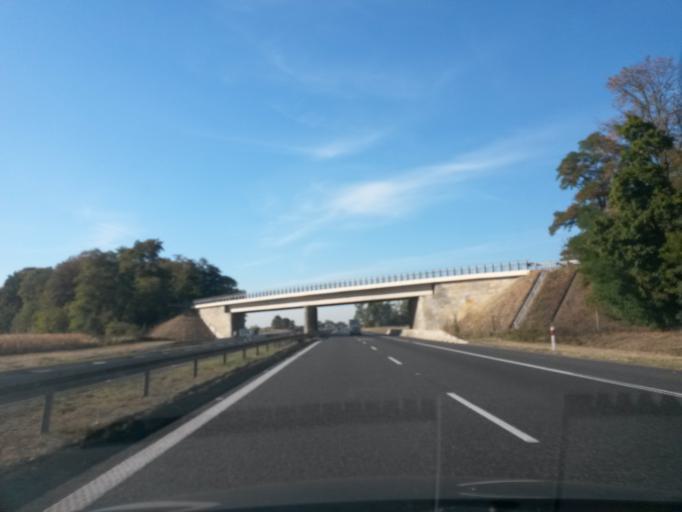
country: PL
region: Lower Silesian Voivodeship
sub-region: Powiat olawski
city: Wierzbno
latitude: 50.9089
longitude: 17.1554
